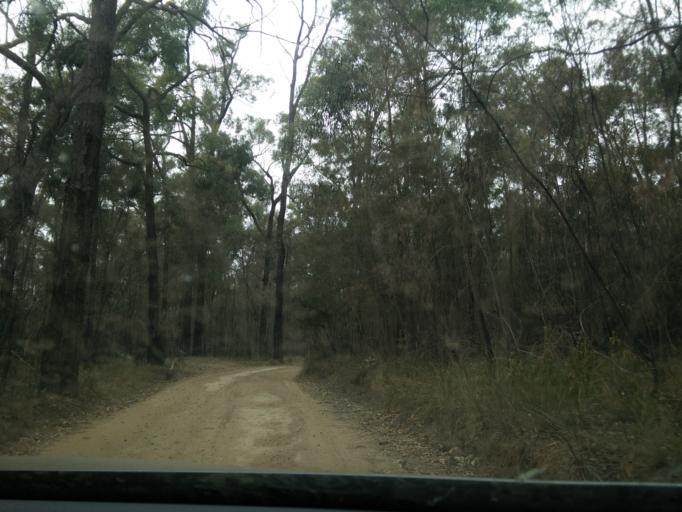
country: AU
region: New South Wales
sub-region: Penrith Municipality
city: Mulgoa
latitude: -33.8325
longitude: 150.5771
